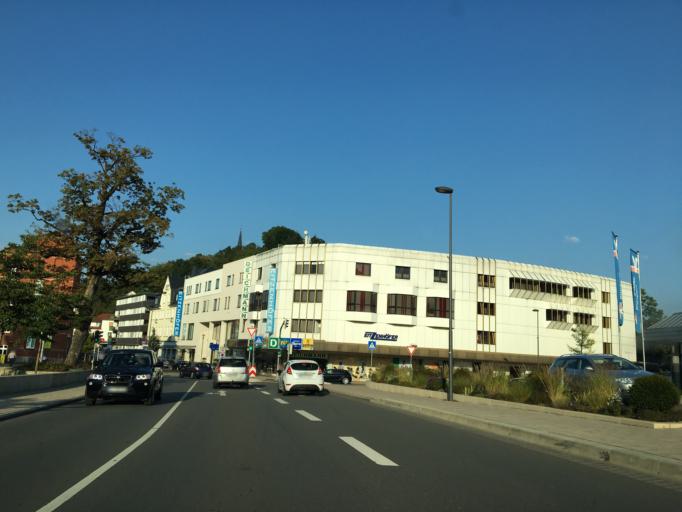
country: DE
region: Hesse
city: Frankenberg
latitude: 51.0564
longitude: 8.7927
